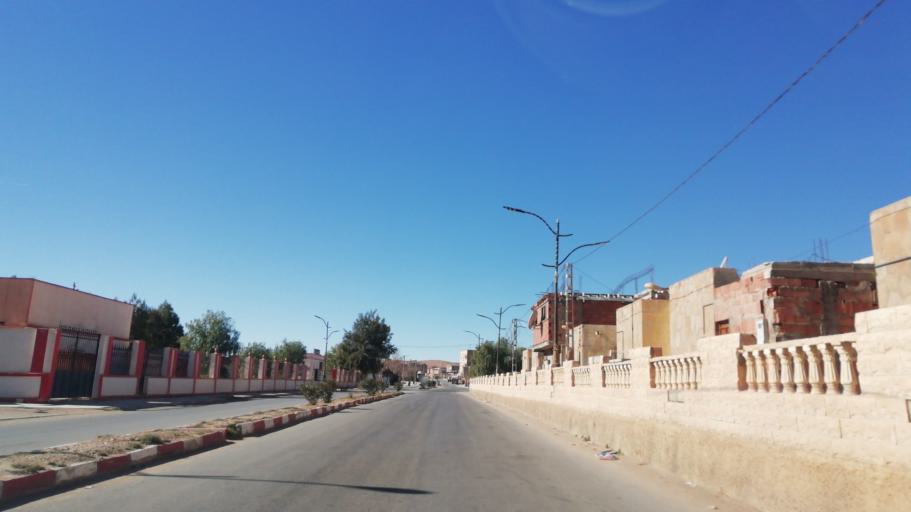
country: DZ
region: El Bayadh
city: El Bayadh
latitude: 33.7284
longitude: 1.5405
